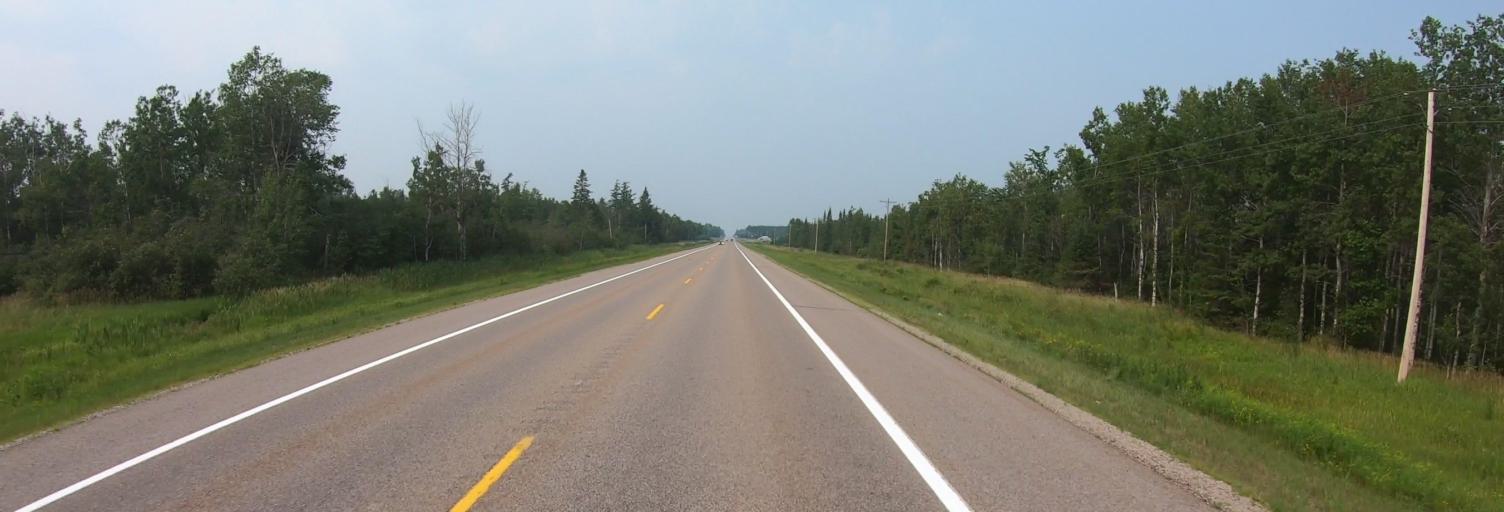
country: US
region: Michigan
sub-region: Chippewa County
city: Sault Ste. Marie
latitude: 46.2754
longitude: -84.3635
